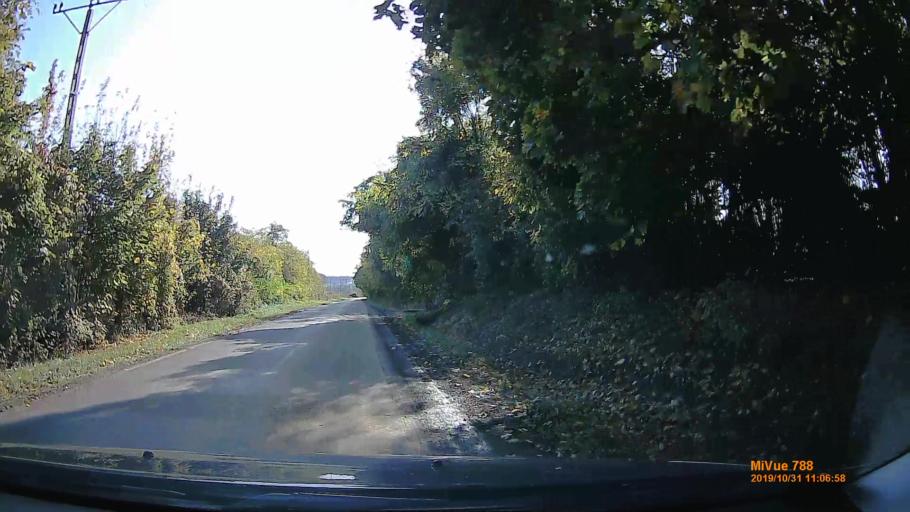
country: HU
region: Pest
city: Pilisborosjeno
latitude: 47.6000
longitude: 18.9958
